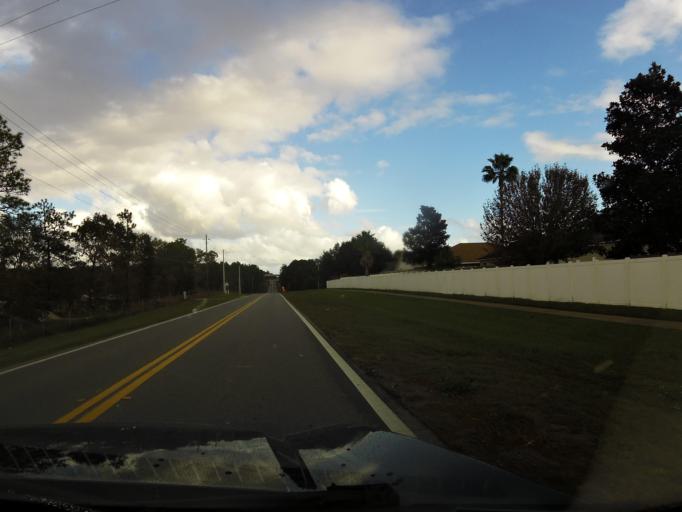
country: US
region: Florida
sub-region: Clay County
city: Asbury Lake
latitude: 30.0462
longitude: -81.7886
